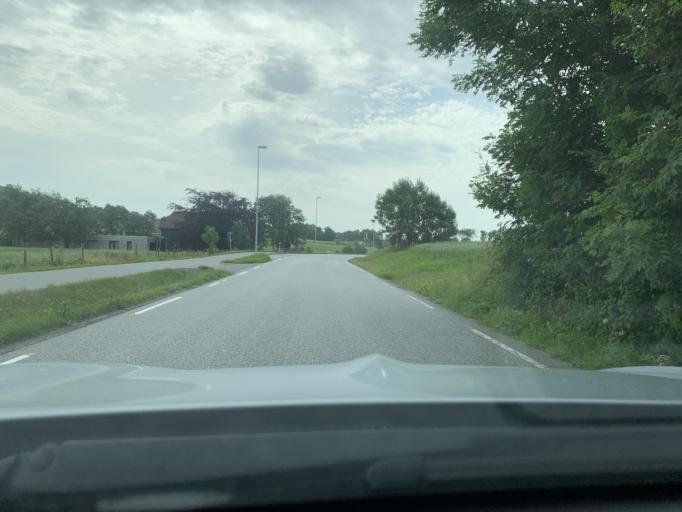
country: NO
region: Rogaland
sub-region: Time
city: Bryne
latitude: 58.7588
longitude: 5.7092
